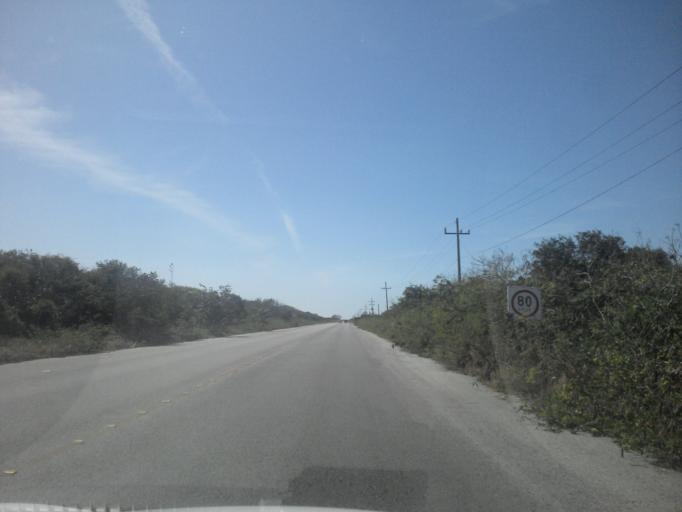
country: MX
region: Yucatan
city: Telchac Puerto
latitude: 21.3329
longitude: -89.3514
